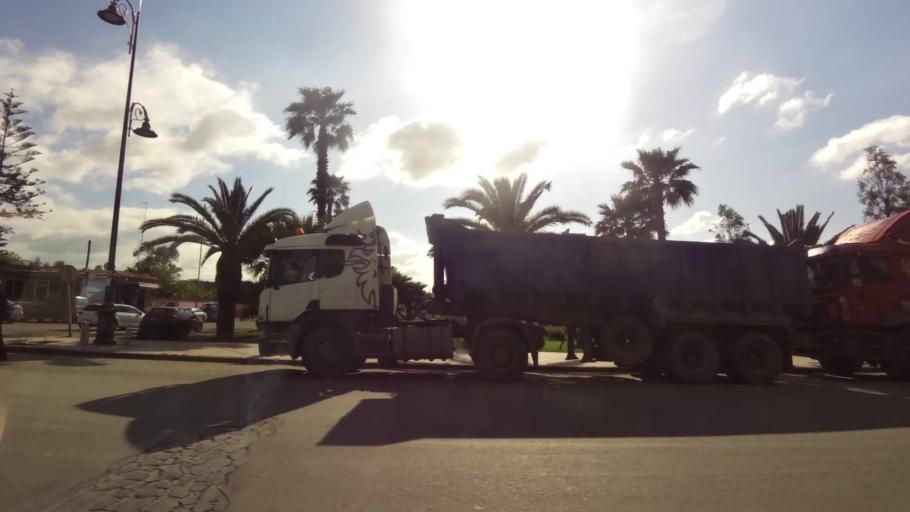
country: MA
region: Chaouia-Ouardigha
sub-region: Settat Province
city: Berrechid
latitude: 33.2635
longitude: -7.5824
